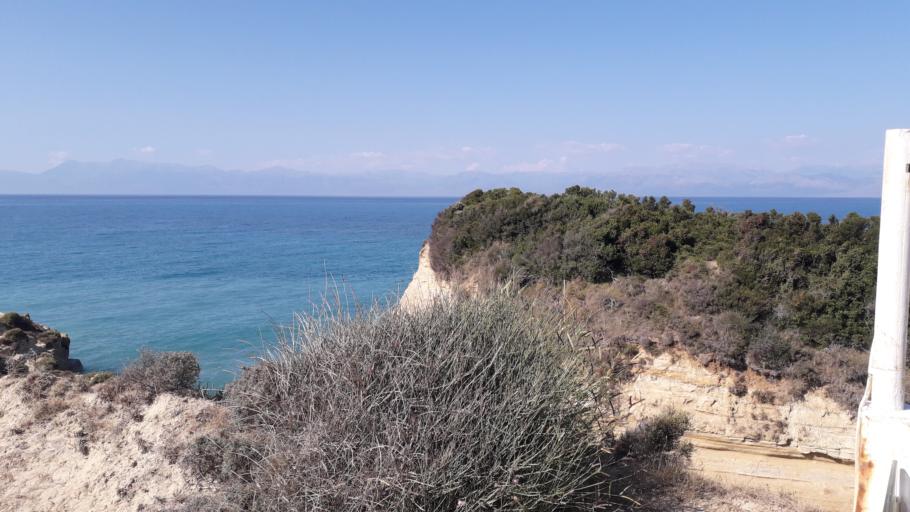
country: GR
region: Ionian Islands
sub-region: Nomos Kerkyras
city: Agios Georgis
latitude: 39.7971
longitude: 19.6978
